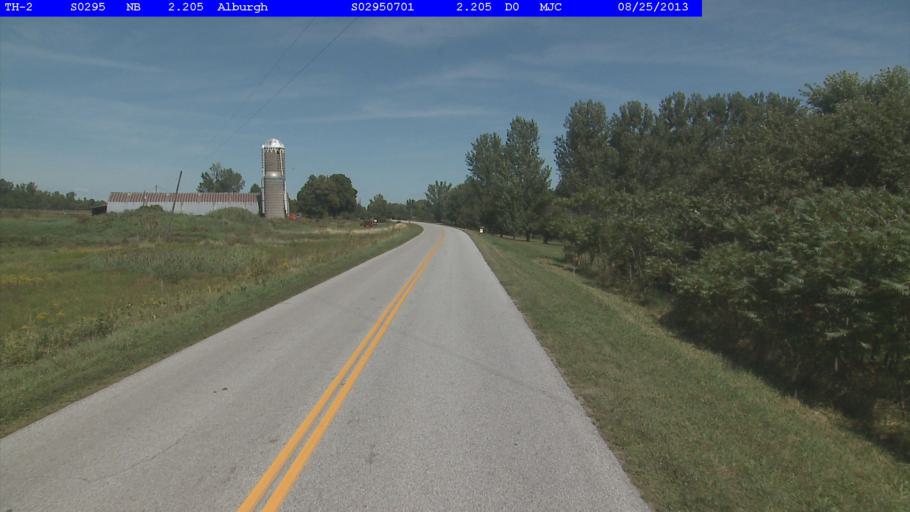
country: US
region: Vermont
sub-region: Franklin County
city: Swanton
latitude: 45.0039
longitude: -73.2154
